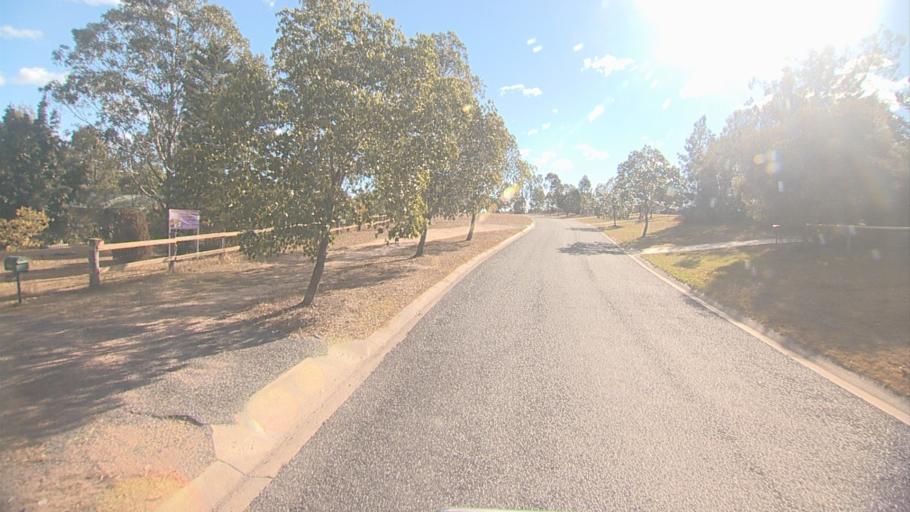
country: AU
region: Queensland
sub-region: Logan
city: North Maclean
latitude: -27.8015
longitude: 152.9661
